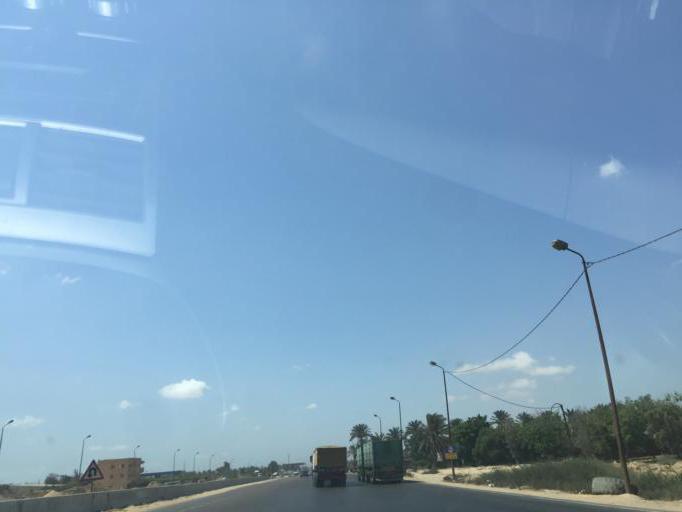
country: EG
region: Alexandria
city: Alexandria
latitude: 30.9797
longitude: 29.8164
